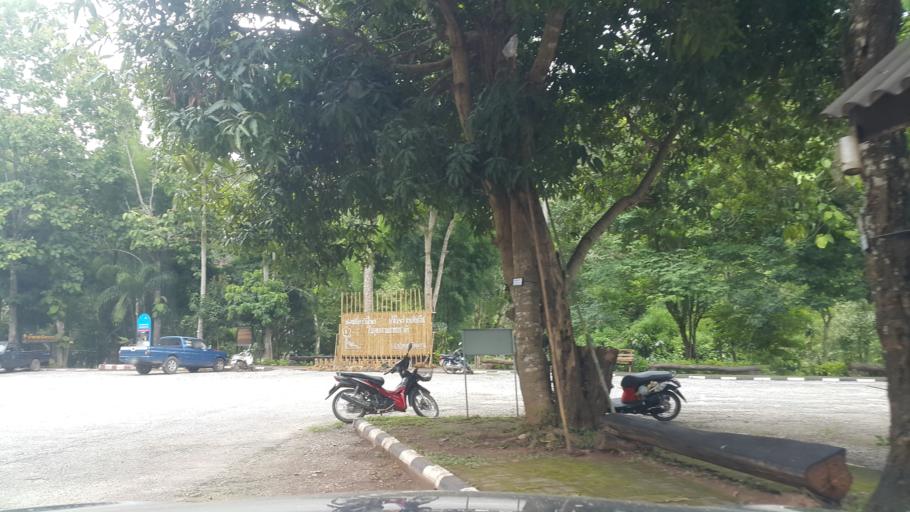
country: TH
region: Phitsanulok
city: Chat Trakan
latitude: 17.2997
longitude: 100.6799
